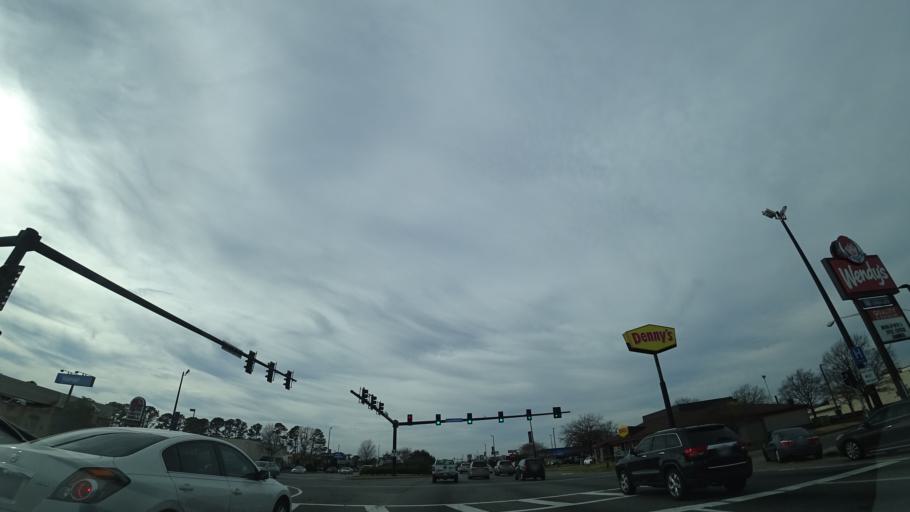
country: US
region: Virginia
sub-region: City of Hampton
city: Hampton
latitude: 37.0434
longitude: -76.3808
